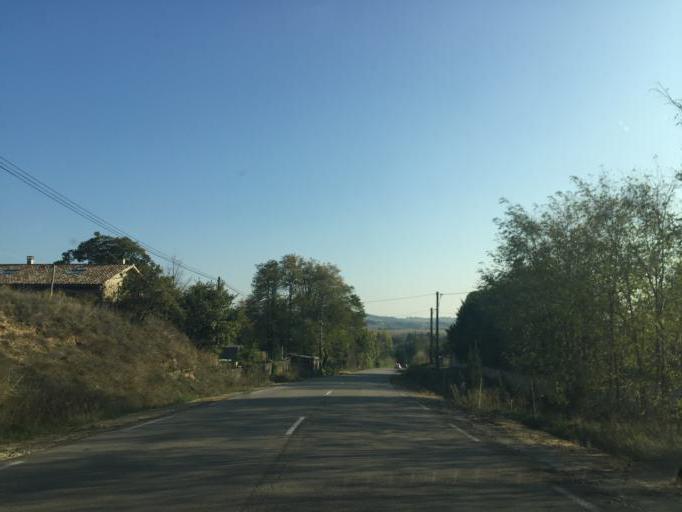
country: FR
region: Rhone-Alpes
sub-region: Departement de la Drome
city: Clerieux
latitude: 45.1232
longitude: 4.9630
